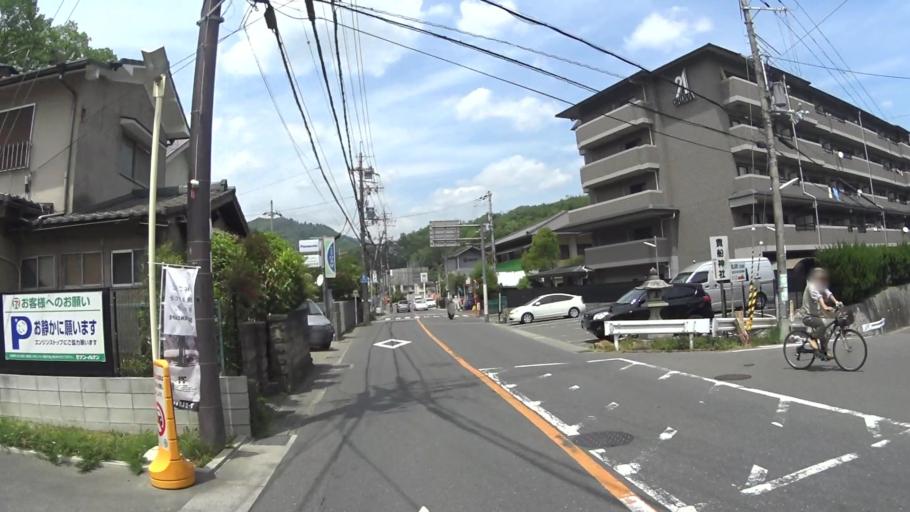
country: JP
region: Kyoto
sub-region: Kyoto-shi
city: Kamigyo-ku
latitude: 35.0774
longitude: 135.7643
